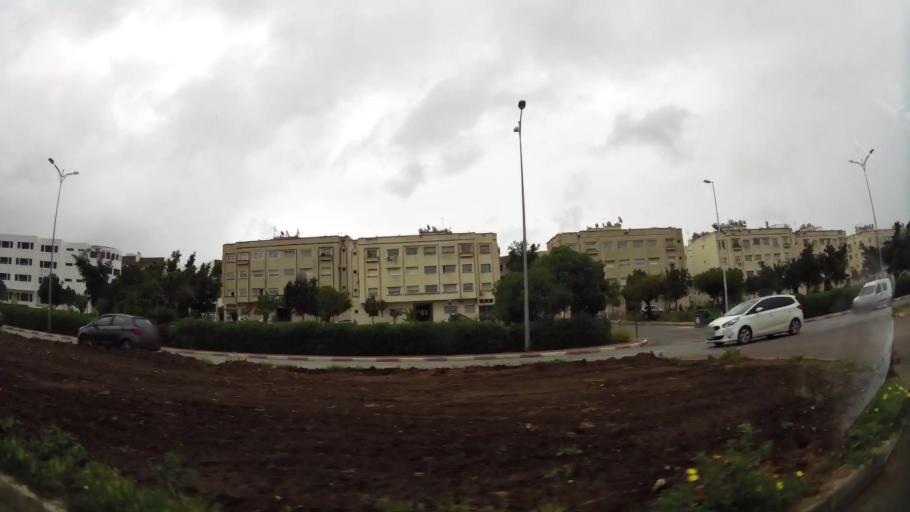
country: MA
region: Grand Casablanca
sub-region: Casablanca
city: Casablanca
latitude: 33.5278
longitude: -7.6170
